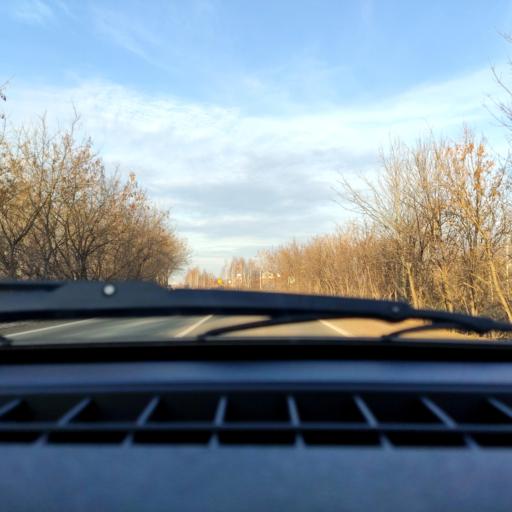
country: RU
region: Bashkortostan
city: Iglino
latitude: 54.7758
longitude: 56.2392
